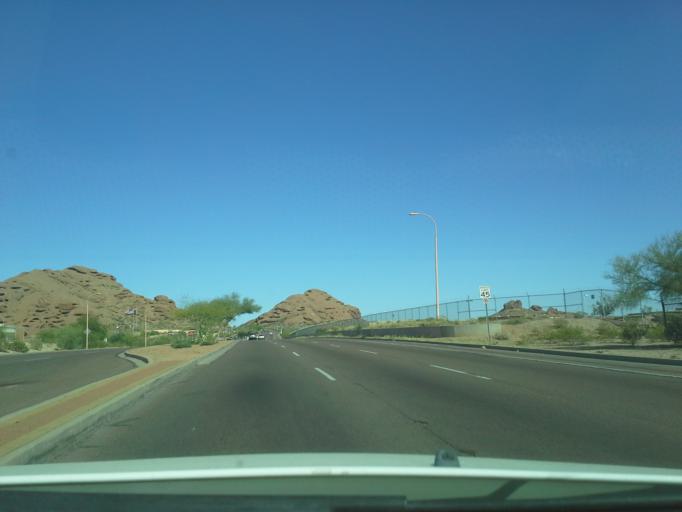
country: US
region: Arizona
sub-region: Maricopa County
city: Tempe Junction
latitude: 33.4655
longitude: -111.9688
